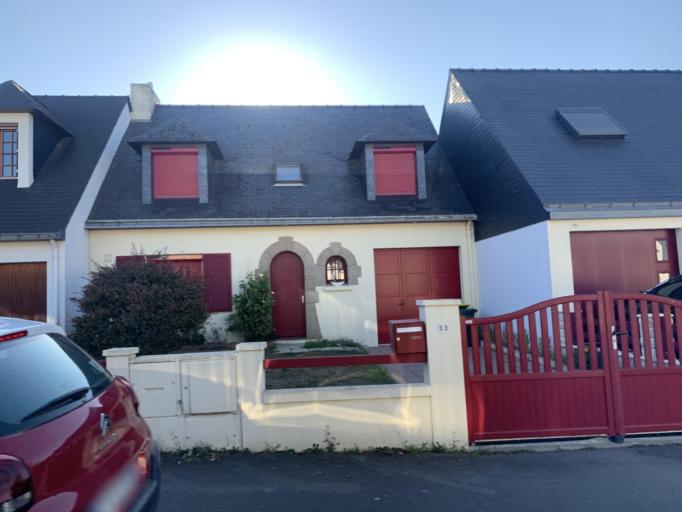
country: FR
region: Pays de la Loire
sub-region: Departement de la Loire-Atlantique
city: Pornichet
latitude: 47.2517
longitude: -2.3114
